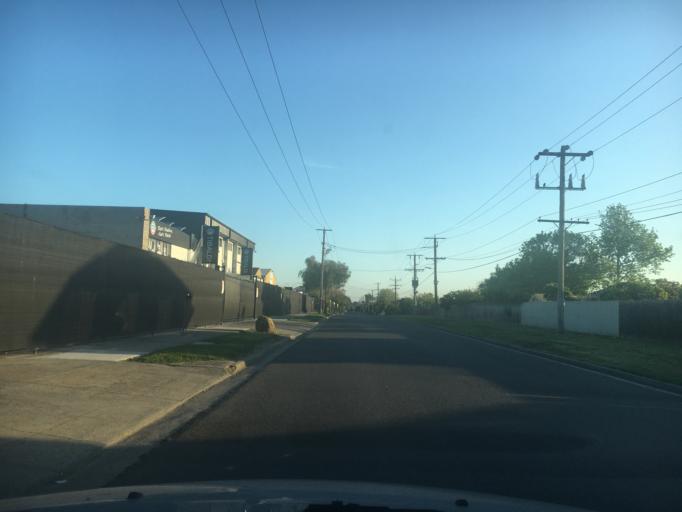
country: AU
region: Victoria
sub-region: Monash
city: Clayton
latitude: -37.9240
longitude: 145.1331
